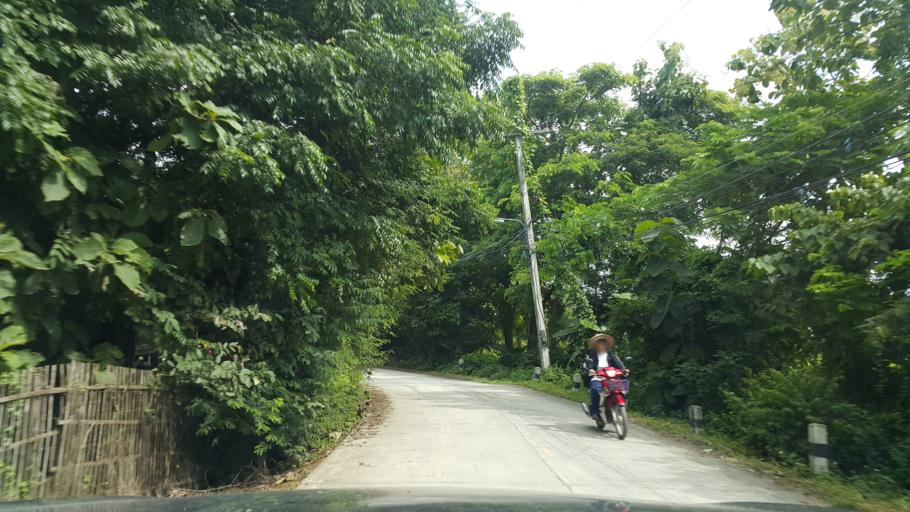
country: TH
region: Chiang Mai
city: San Kamphaeng
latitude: 18.7956
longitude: 99.1435
